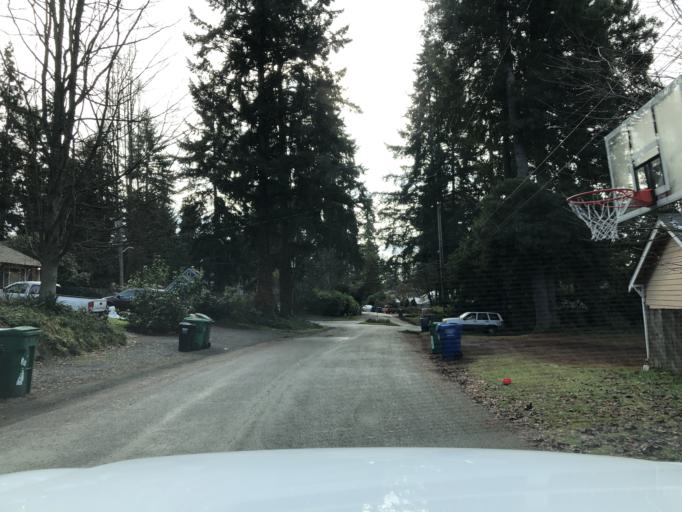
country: US
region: Washington
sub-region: King County
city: Lake Forest Park
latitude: 47.7290
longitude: -122.3045
